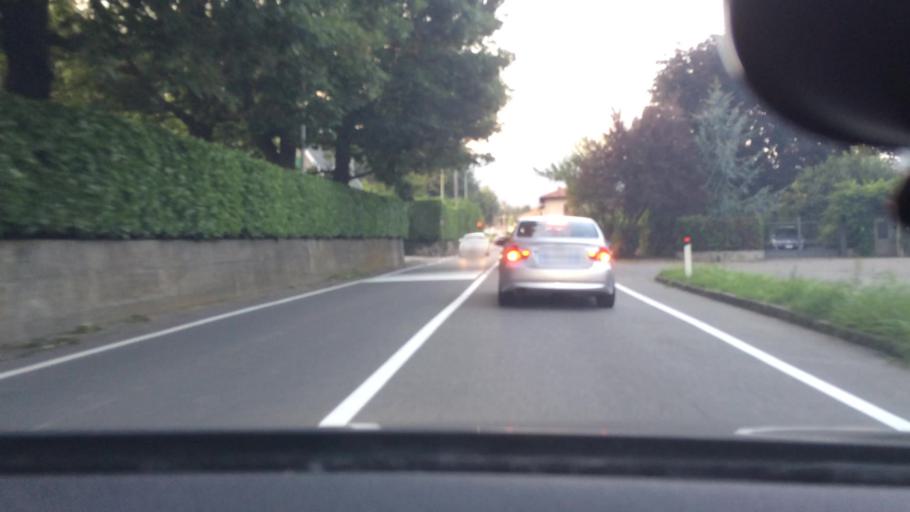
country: IT
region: Lombardy
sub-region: Provincia di Como
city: Anzano del Parco
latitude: 45.7738
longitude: 9.1937
